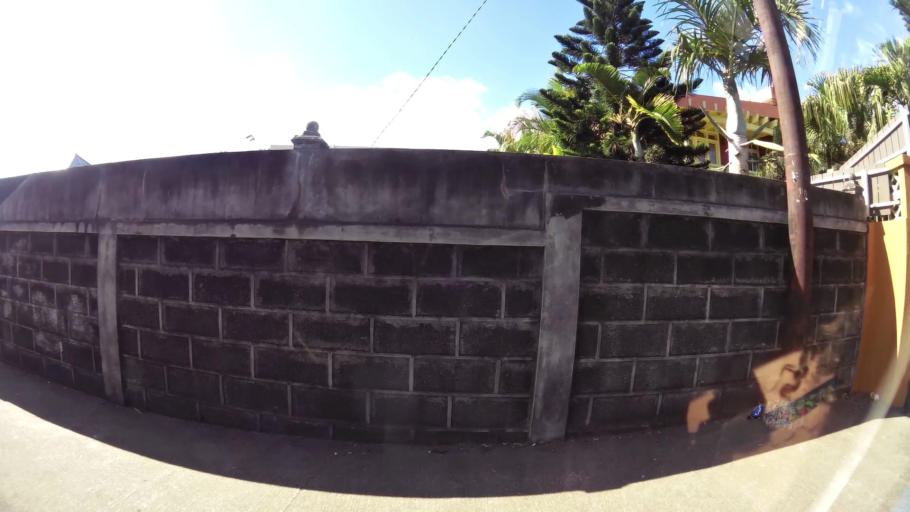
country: MU
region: Plaines Wilhems
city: Vacoas
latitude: -20.3197
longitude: 57.4846
